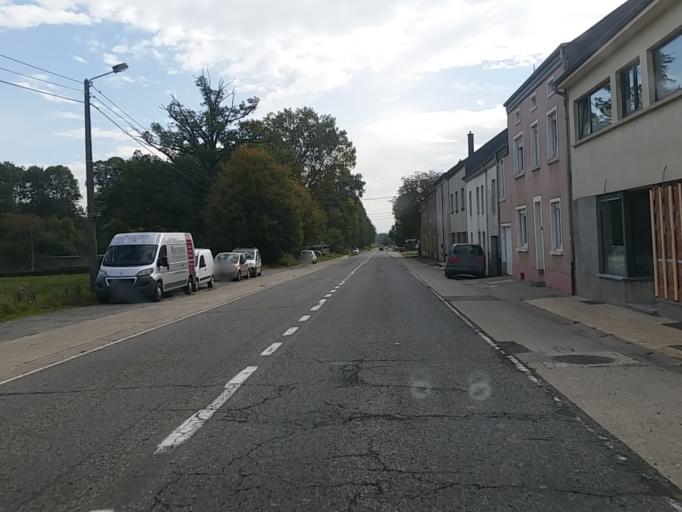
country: BE
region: Wallonia
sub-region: Province du Luxembourg
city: Etalle
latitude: 49.6747
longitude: 5.5636
